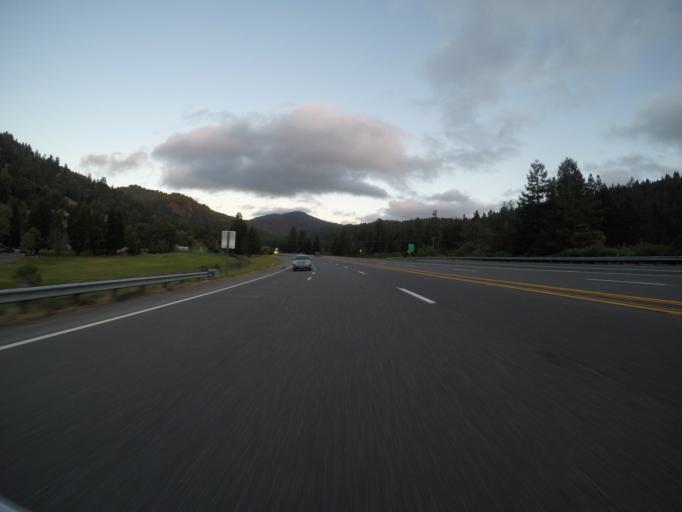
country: US
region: California
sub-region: Humboldt County
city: Redway
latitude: 40.0672
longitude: -123.7883
